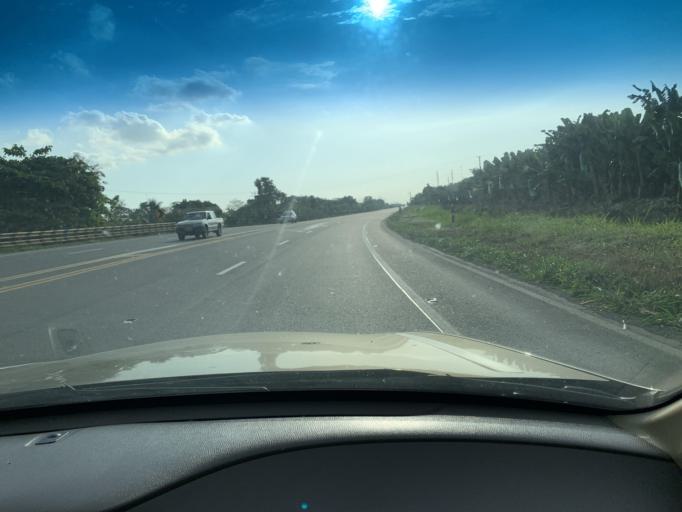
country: EC
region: Guayas
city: Naranjito
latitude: -2.2576
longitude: -79.5649
